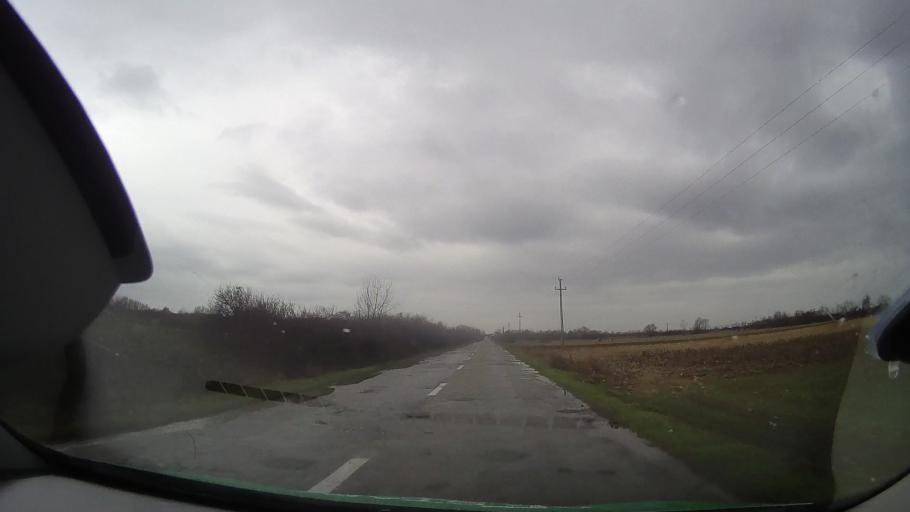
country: RO
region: Bihor
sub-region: Comuna Soimi
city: Soimi
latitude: 46.6912
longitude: 22.1007
